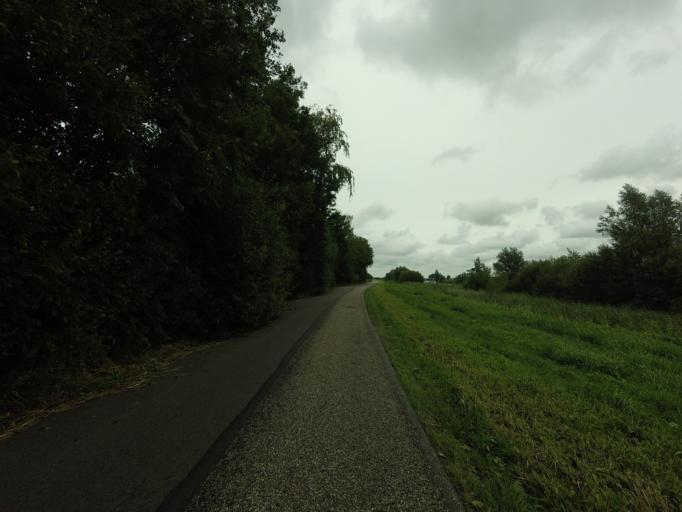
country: NL
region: Overijssel
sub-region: Gemeente Steenwijkerland
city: Oldemarkt
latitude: 52.8217
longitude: 5.9176
